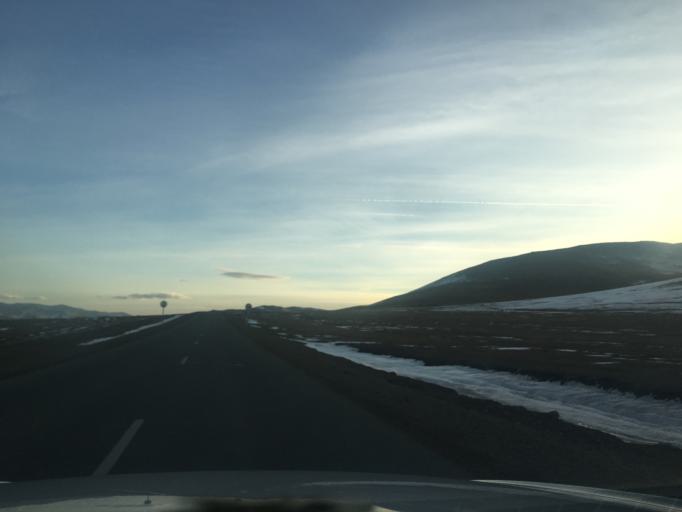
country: MN
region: Central Aimak
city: Mandal
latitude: 48.2263
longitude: 106.7160
